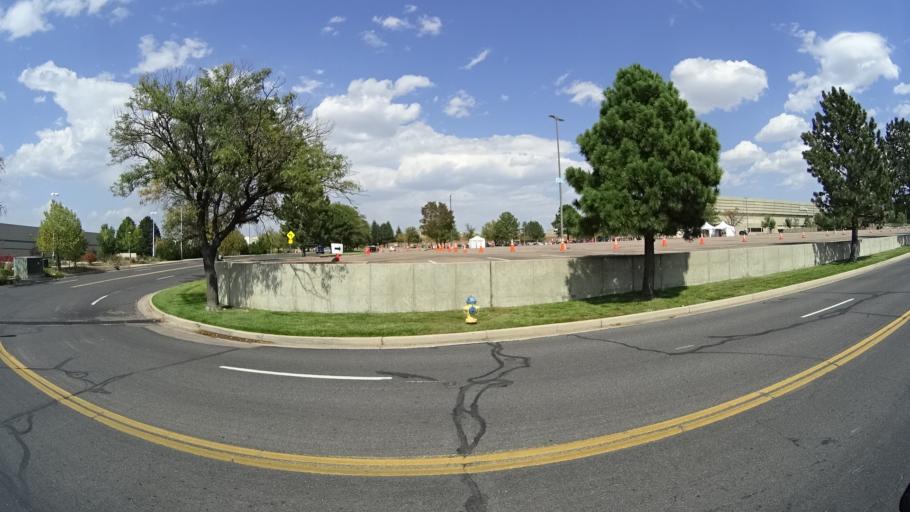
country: US
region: Colorado
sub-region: El Paso County
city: Colorado Springs
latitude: 38.8409
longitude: -104.7638
